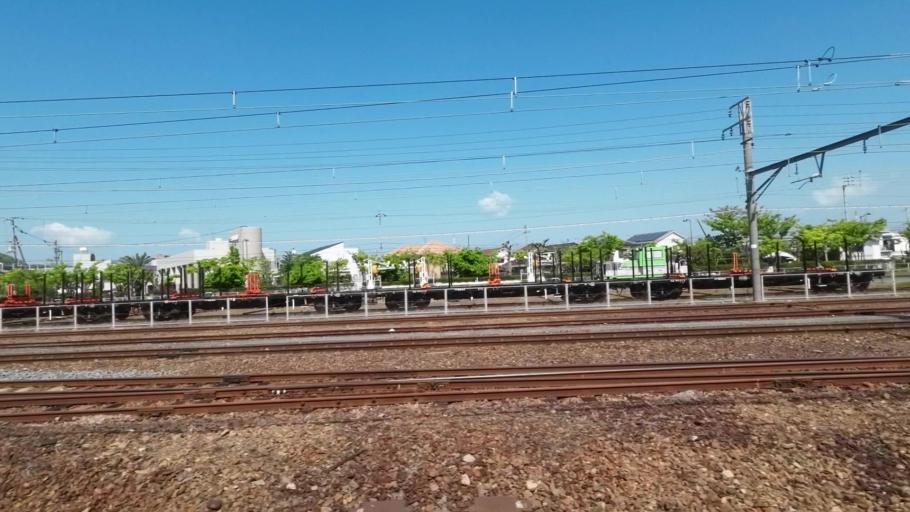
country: JP
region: Kagawa
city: Tadotsu
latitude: 34.2730
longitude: 133.7583
